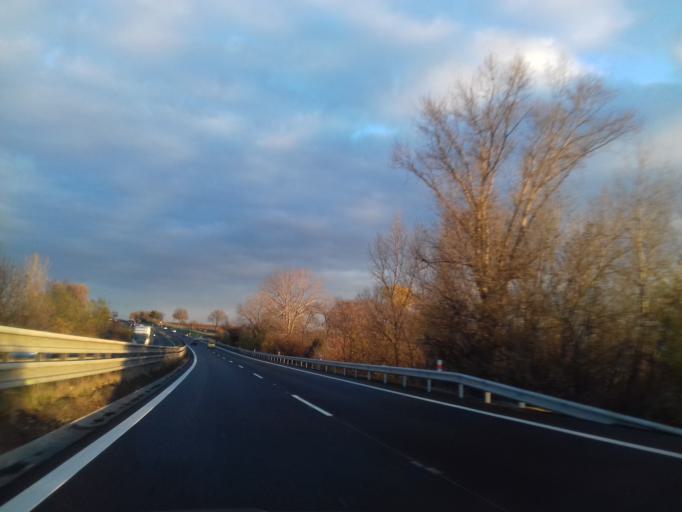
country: CZ
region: Olomoucky
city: Urcice
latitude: 49.4123
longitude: 17.1110
